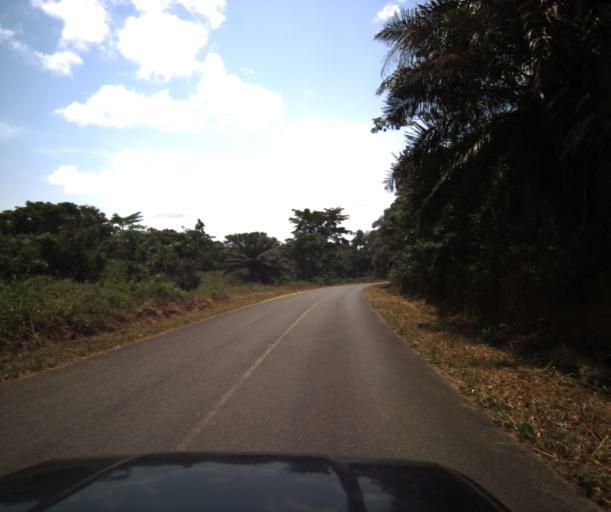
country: CM
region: Centre
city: Eseka
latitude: 3.6951
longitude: 10.7864
